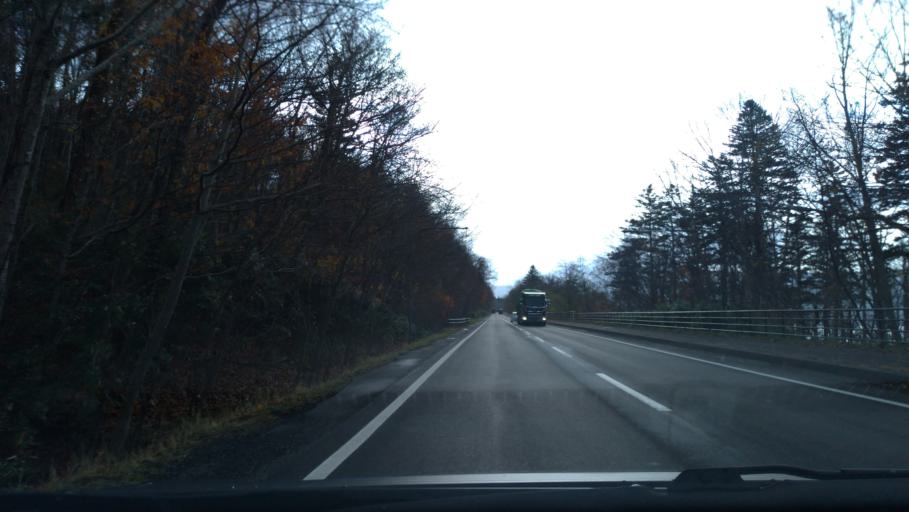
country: JP
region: Hokkaido
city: Shiraoi
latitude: 42.7241
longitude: 141.3314
